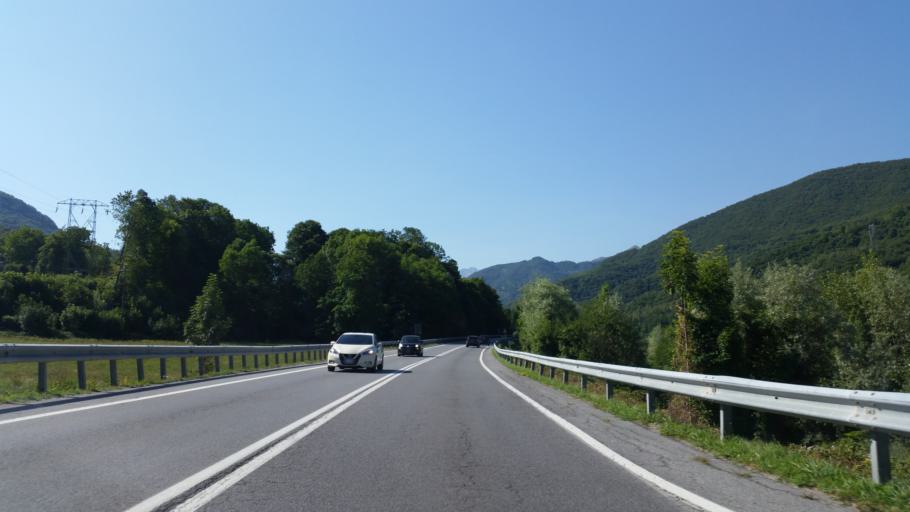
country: IT
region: Piedmont
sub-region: Provincia di Cuneo
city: Robilante
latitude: 44.2870
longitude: 7.5194
